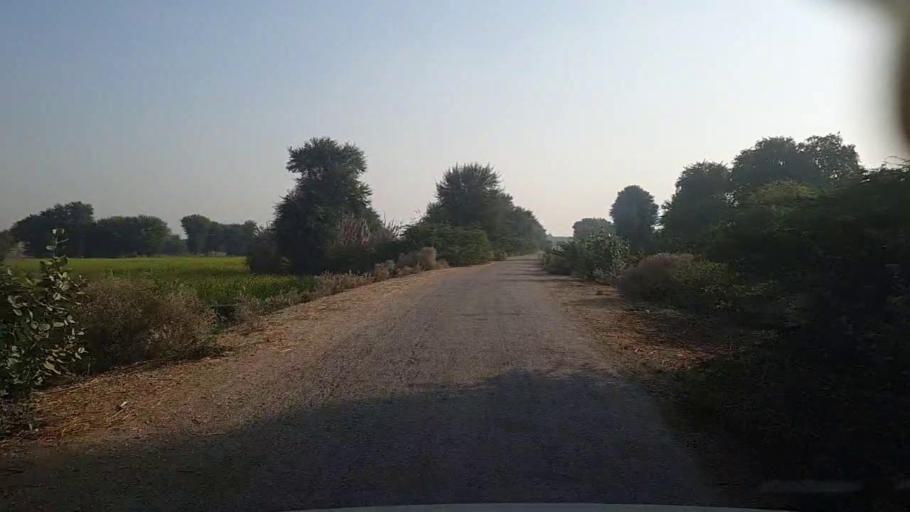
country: PK
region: Sindh
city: Karaundi
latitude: 26.7475
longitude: 68.4769
